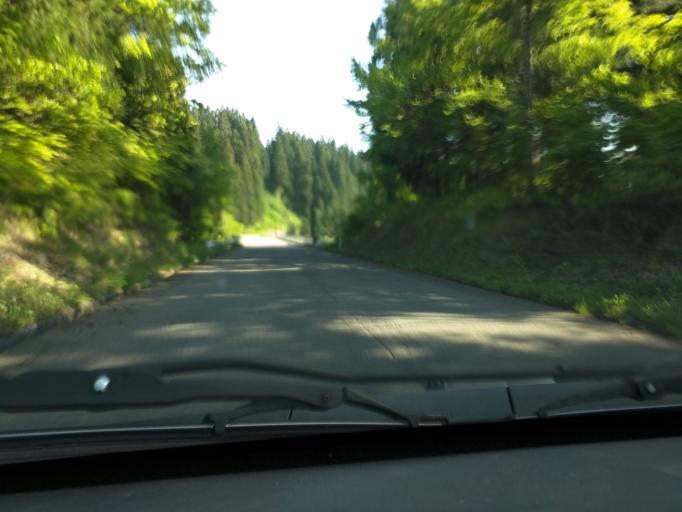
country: JP
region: Fukushima
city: Kitakata
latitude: 37.4802
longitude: 139.6697
